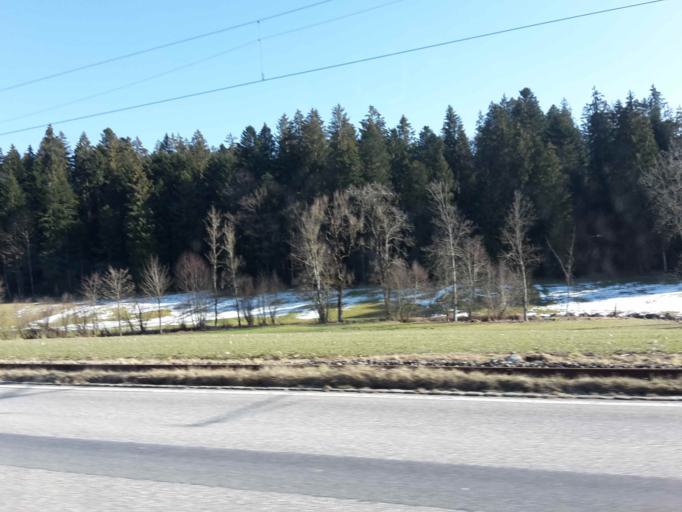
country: CH
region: Bern
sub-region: Emmental District
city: Durrenroth
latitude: 47.0887
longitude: 7.7684
